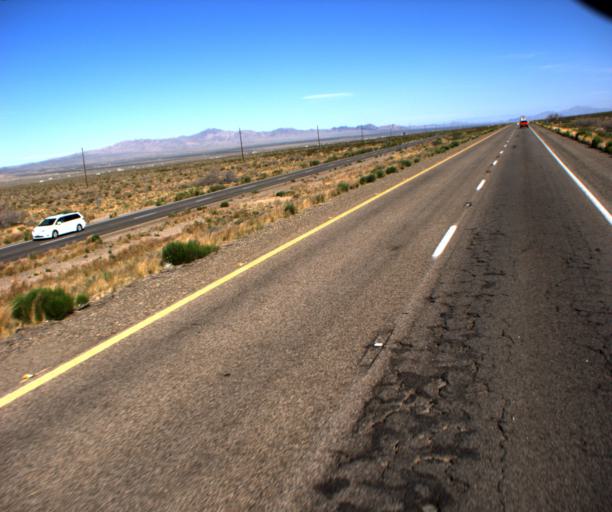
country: US
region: Arizona
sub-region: Mohave County
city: Dolan Springs
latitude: 35.4675
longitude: -114.3092
